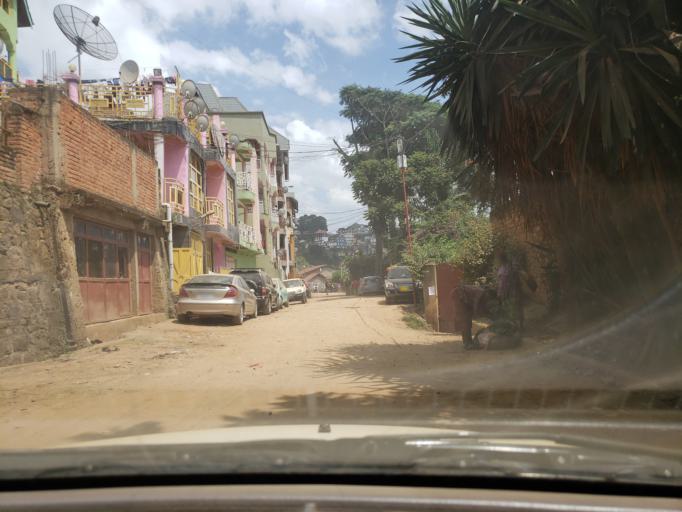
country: CD
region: South Kivu
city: Bukavu
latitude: -2.4989
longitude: 28.8659
